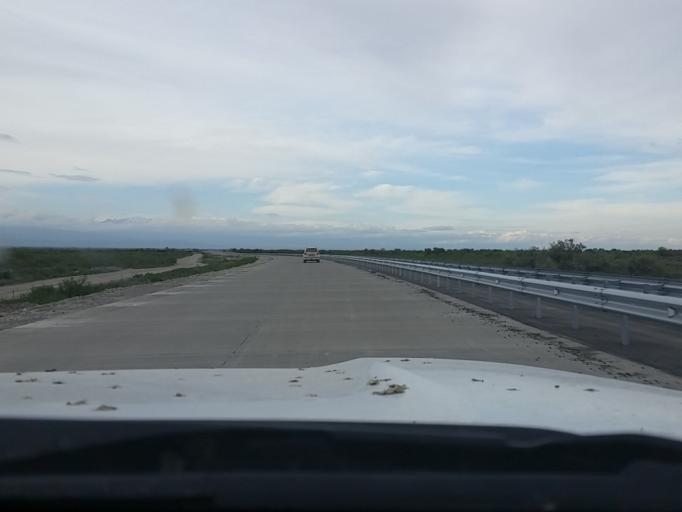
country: KZ
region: Almaty Oblysy
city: Zharkent
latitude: 44.0600
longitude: 80.0230
